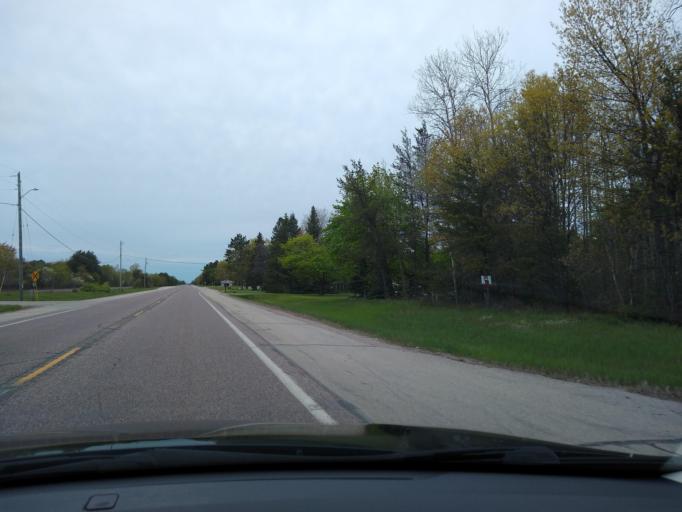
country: US
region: Michigan
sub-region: Delta County
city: Gladstone
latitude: 45.8638
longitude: -87.0628
